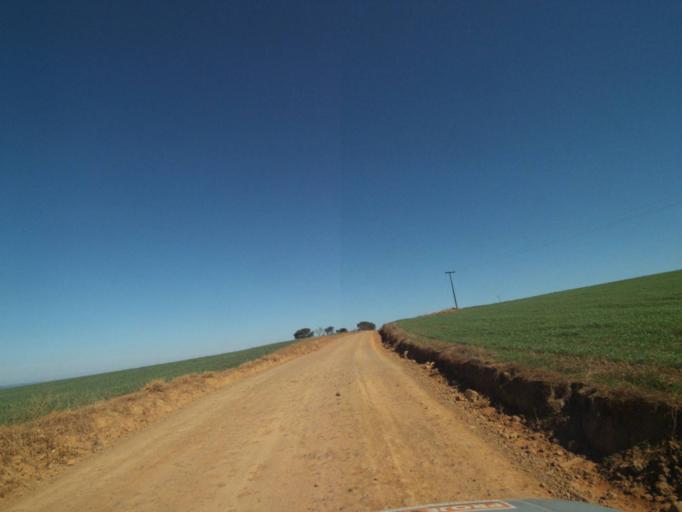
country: BR
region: Parana
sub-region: Tibagi
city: Tibagi
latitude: -24.6177
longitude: -50.6077
